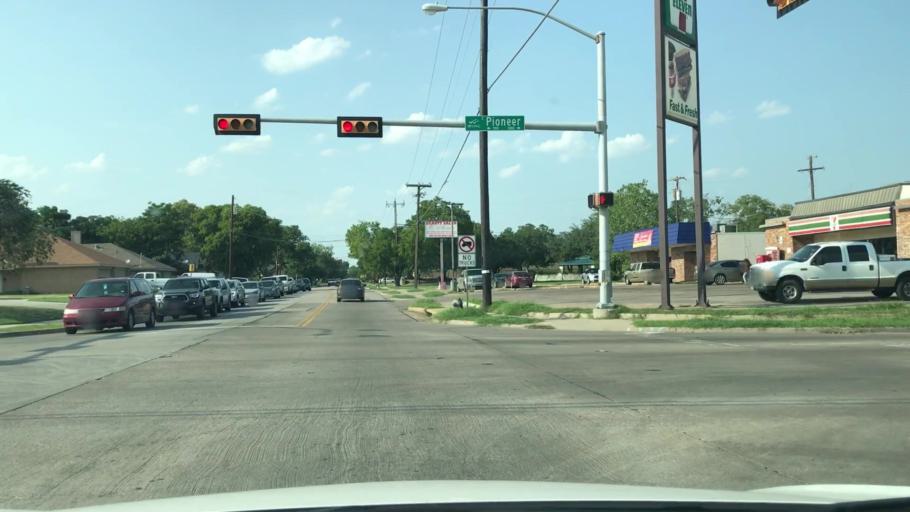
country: US
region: Texas
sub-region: Dallas County
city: Irving
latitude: 32.8176
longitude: -96.9343
